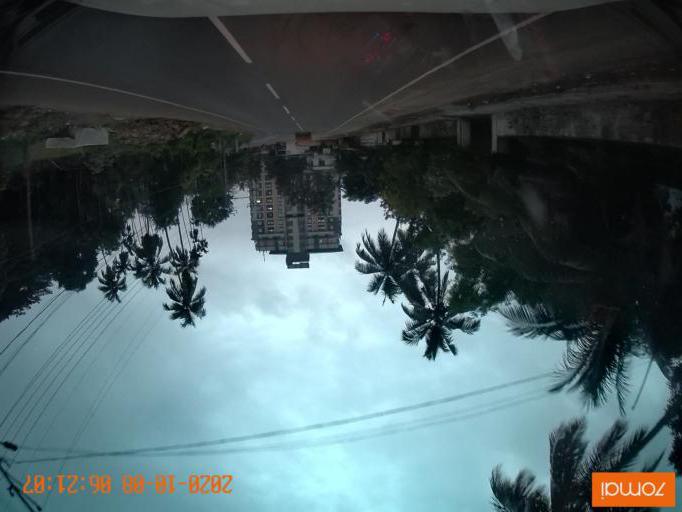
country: IN
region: Kerala
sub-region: Thrissur District
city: Trichur
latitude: 10.5197
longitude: 76.2339
